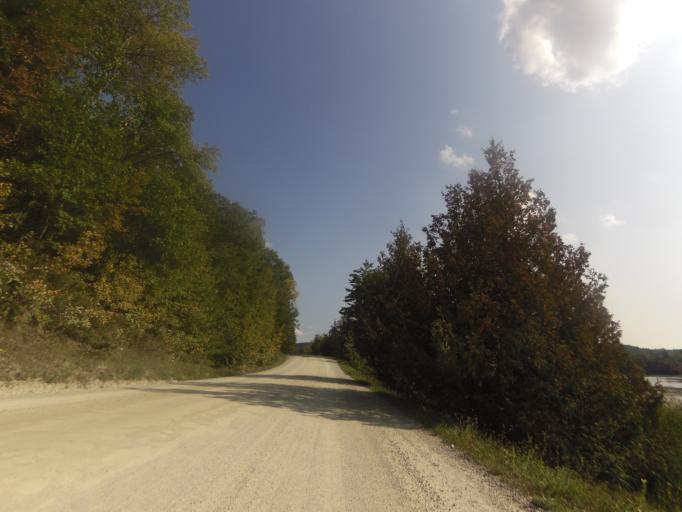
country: CA
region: Ontario
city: Renfrew
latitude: 45.1354
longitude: -76.6446
